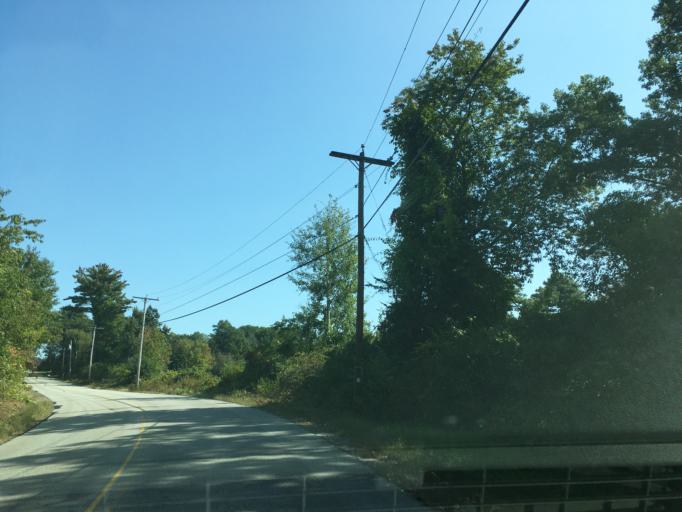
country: US
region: New Hampshire
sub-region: Rockingham County
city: Exeter
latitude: 43.0030
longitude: -70.9038
